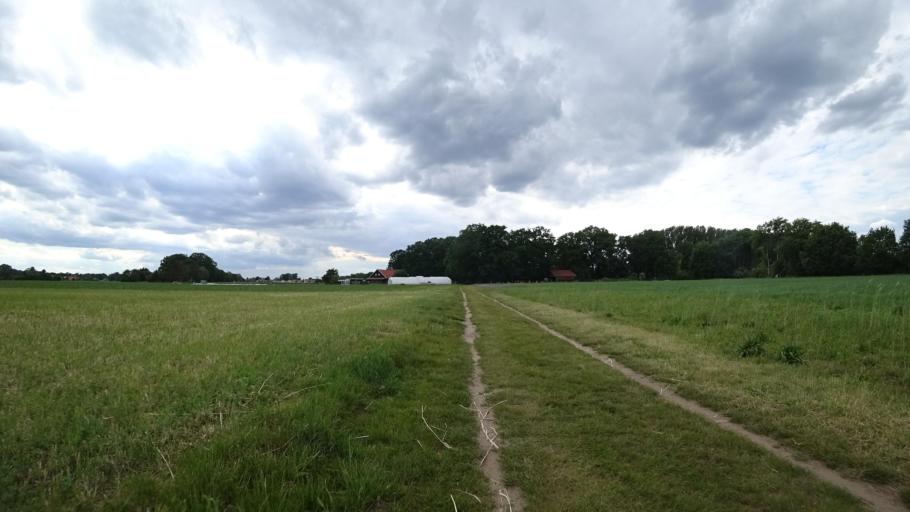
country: DE
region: North Rhine-Westphalia
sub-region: Regierungsbezirk Detmold
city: Guetersloh
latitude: 51.8947
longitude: 8.4260
